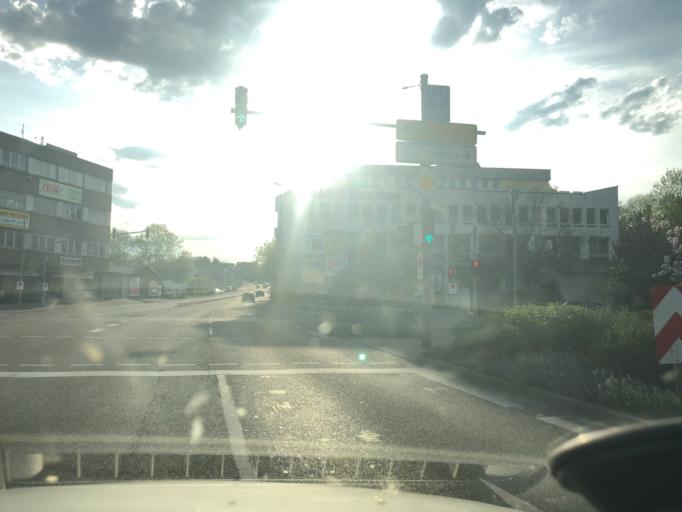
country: DE
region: Baden-Wuerttemberg
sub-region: Regierungsbezirk Stuttgart
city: Ditzingen
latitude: 48.8232
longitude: 9.0731
